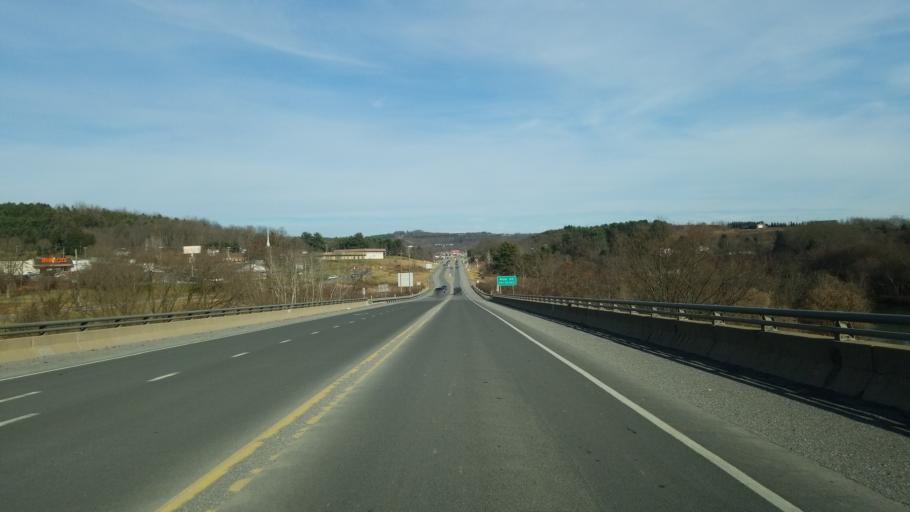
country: US
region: Pennsylvania
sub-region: Clearfield County
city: Clearfield
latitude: 41.0257
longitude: -78.4142
